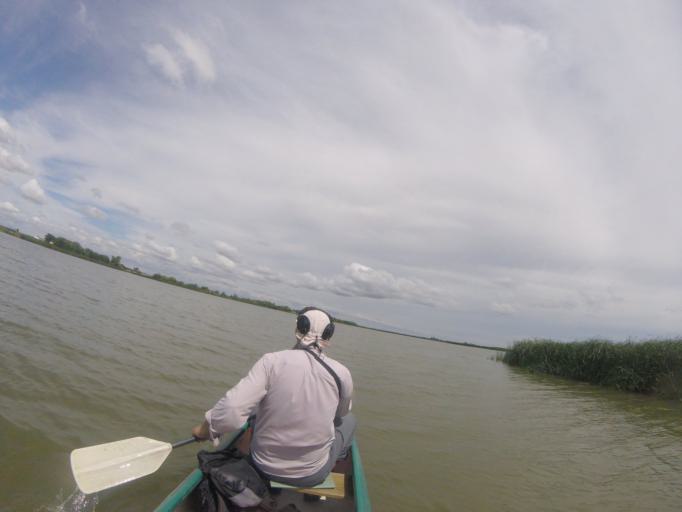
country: HU
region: Heves
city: Poroszlo
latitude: 47.5877
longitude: 20.6252
